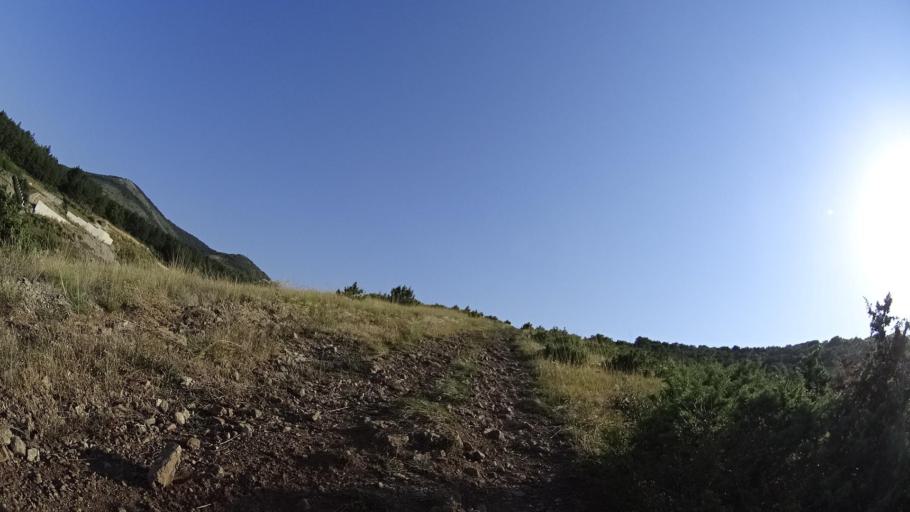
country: BG
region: Plovdiv
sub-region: Obshtina Plovdiv
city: Plovdiv
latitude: 42.0620
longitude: 24.6946
